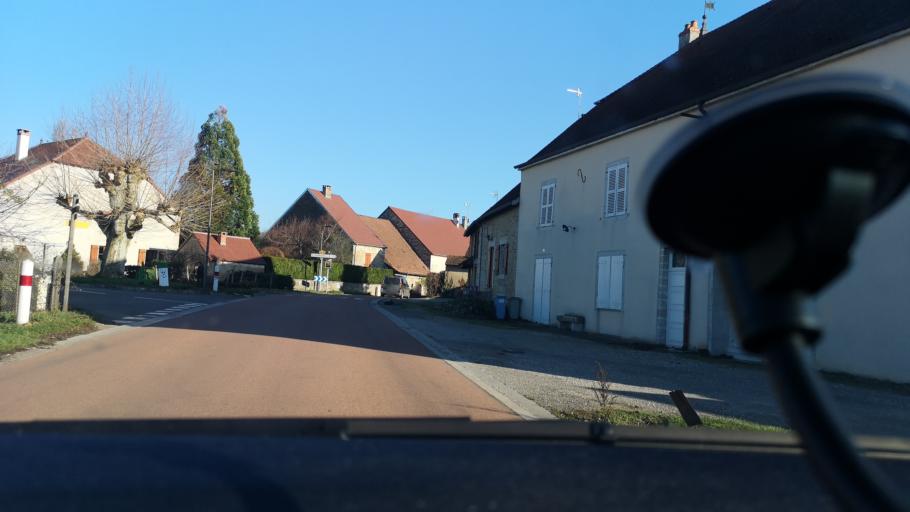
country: FR
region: Franche-Comte
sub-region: Departement du Jura
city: Bletterans
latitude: 46.7613
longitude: 5.5208
